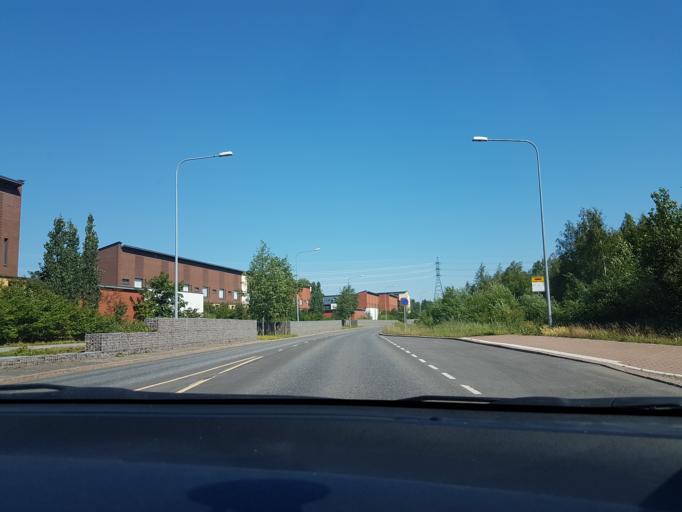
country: FI
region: Uusimaa
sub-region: Helsinki
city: Vantaa
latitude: 60.2296
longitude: 25.1340
